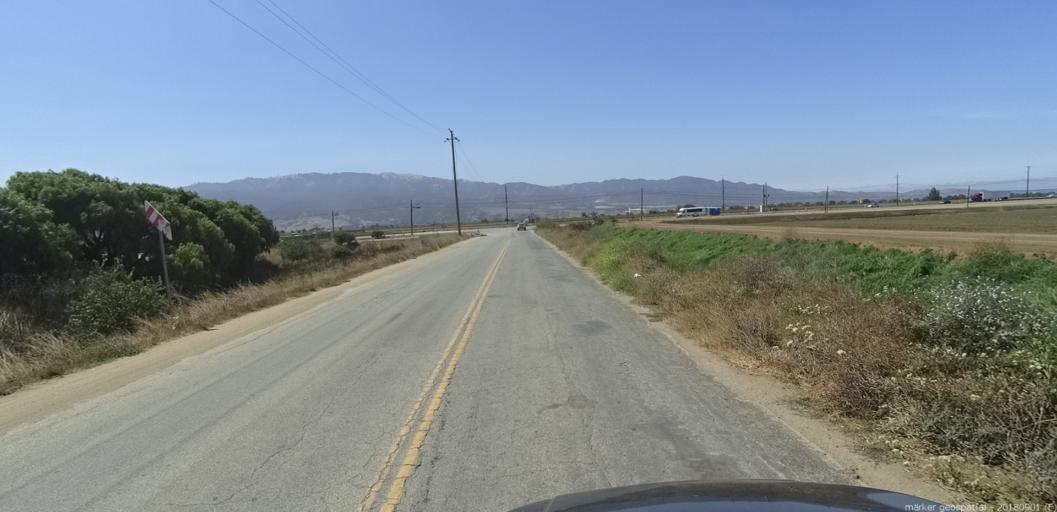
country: US
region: California
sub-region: Monterey County
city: Chualar
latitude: 36.6066
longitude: -121.5558
